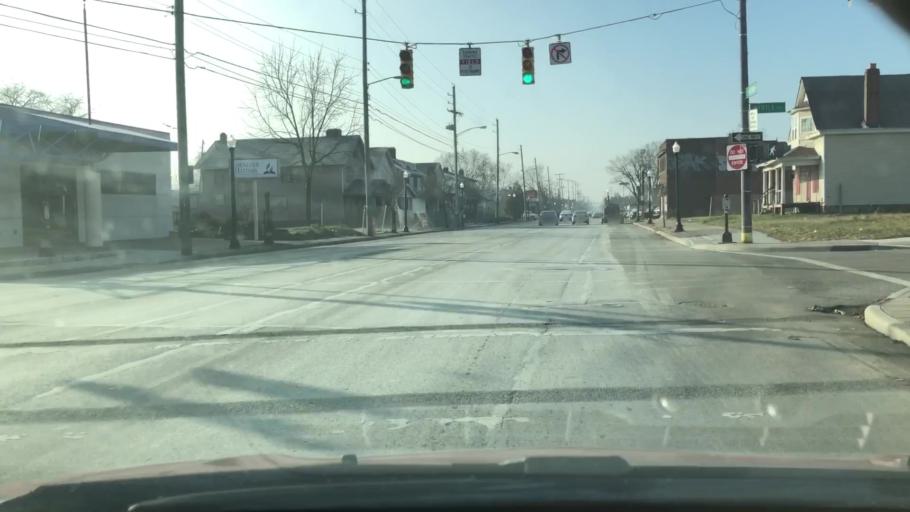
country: US
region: Ohio
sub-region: Franklin County
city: Bexley
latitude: 40.0171
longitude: -82.9654
